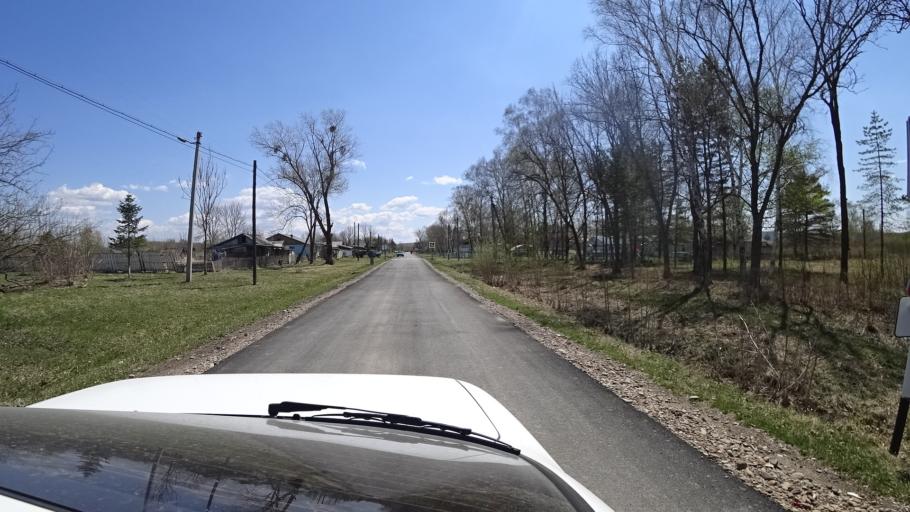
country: RU
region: Primorskiy
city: Dal'nerechensk
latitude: 45.7966
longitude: 133.7676
